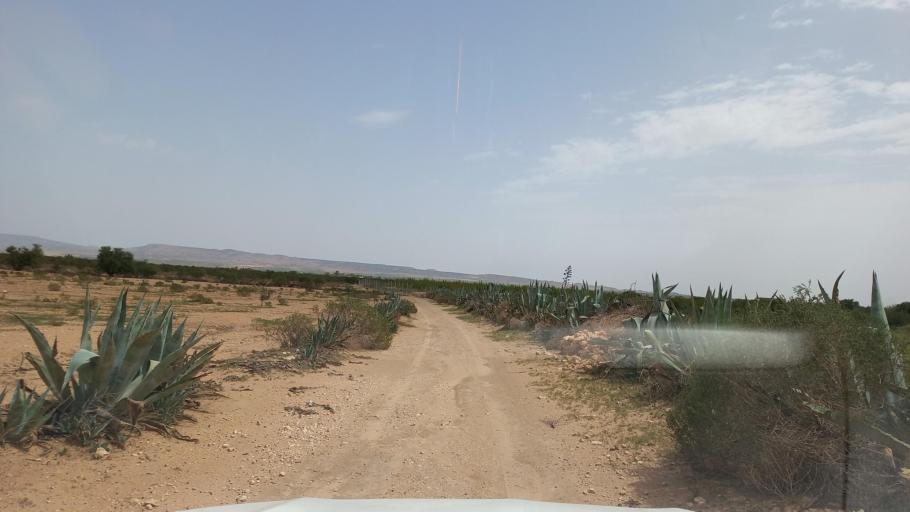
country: TN
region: Al Qasrayn
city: Kasserine
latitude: 35.2927
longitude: 9.0073
